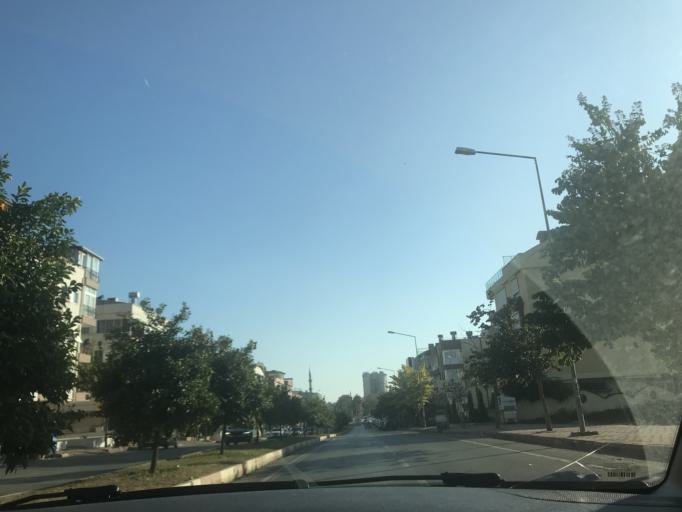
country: TR
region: Antalya
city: Antalya
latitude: 36.8859
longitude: 30.6475
